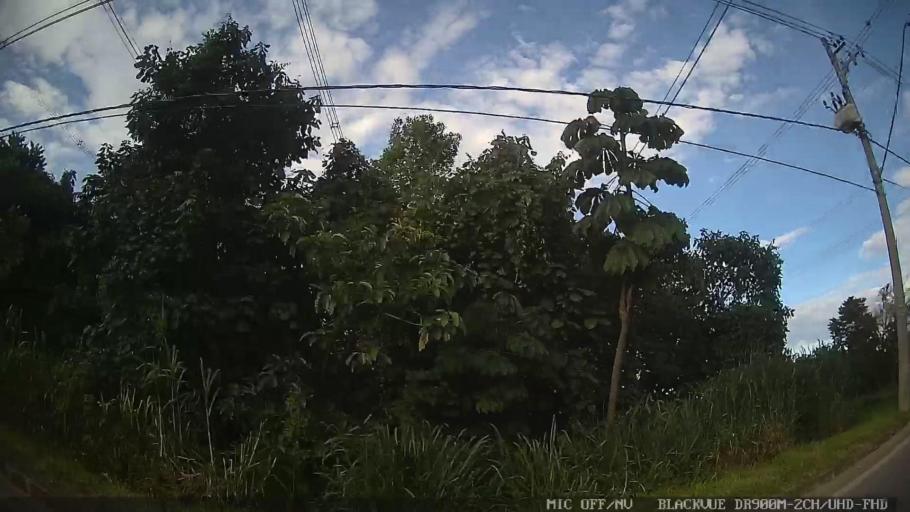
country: BR
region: Sao Paulo
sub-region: Mogi das Cruzes
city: Mogi das Cruzes
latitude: -23.5564
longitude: -46.1469
